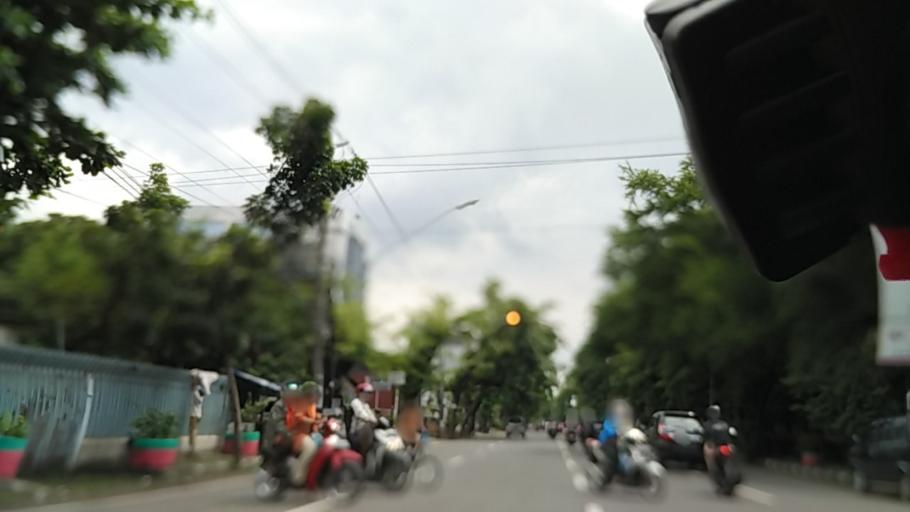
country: ID
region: Central Java
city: Semarang
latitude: -6.9813
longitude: 110.4350
